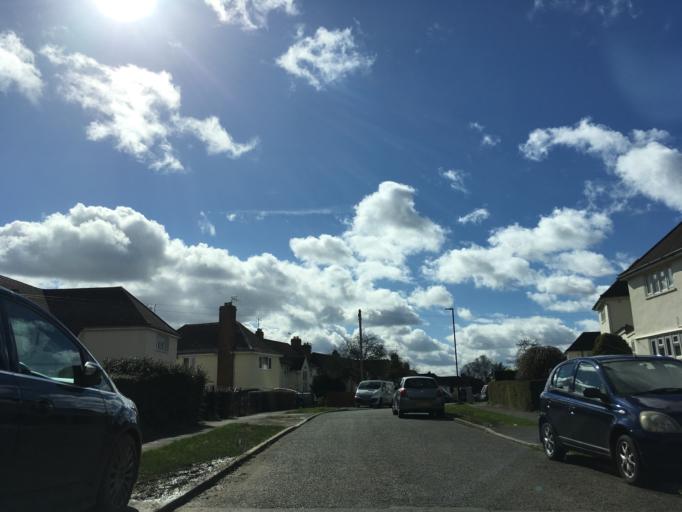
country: GB
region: England
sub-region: Gloucestershire
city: Wotton-under-Edge
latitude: 51.6370
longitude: -2.3447
